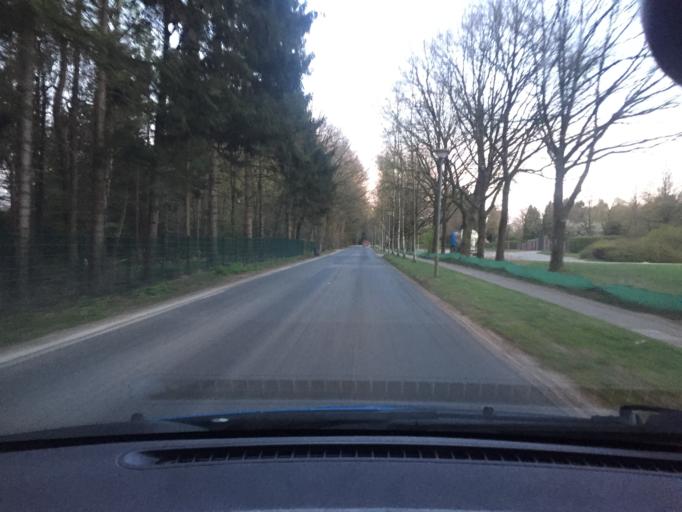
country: DE
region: Lower Saxony
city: Buchholz in der Nordheide
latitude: 53.3055
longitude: 9.8691
